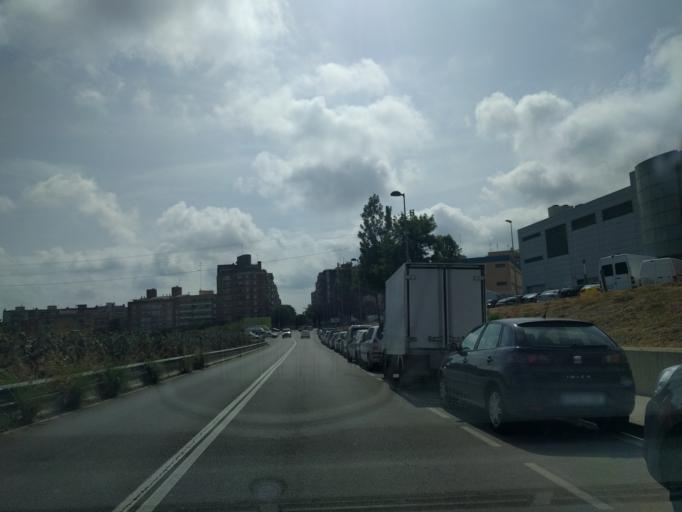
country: ES
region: Catalonia
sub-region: Provincia de Barcelona
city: Mataro
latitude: 41.5502
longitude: 2.4544
